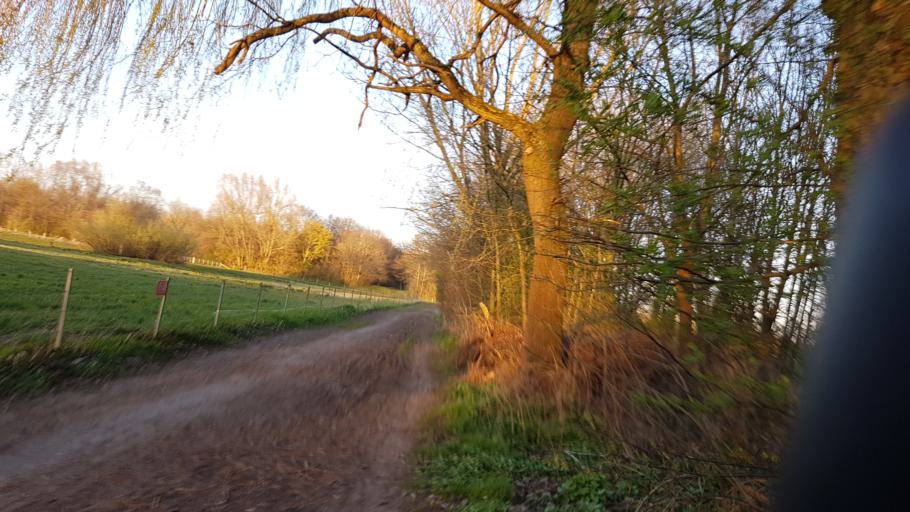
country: DE
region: Lower Saxony
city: Laatzen
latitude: 52.3073
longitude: 9.7871
